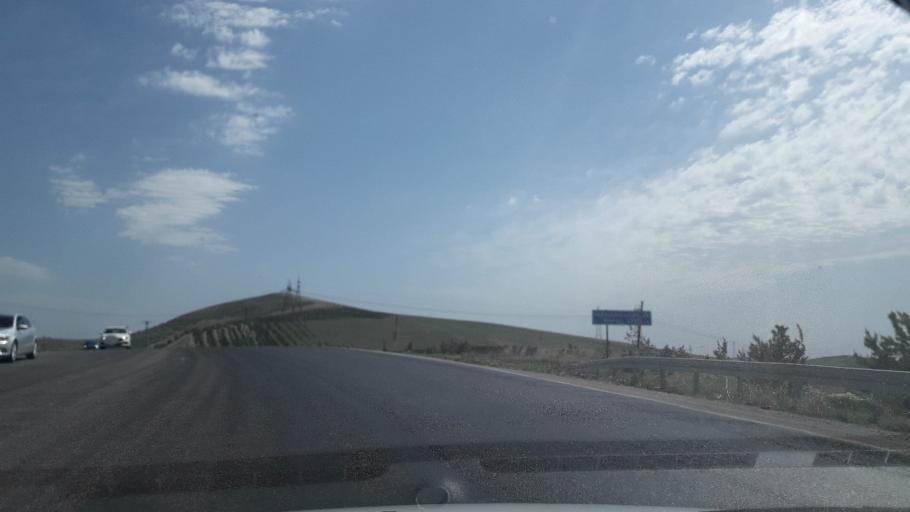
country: TR
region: Sivas
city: Deliktas
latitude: 39.3215
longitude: 37.1416
